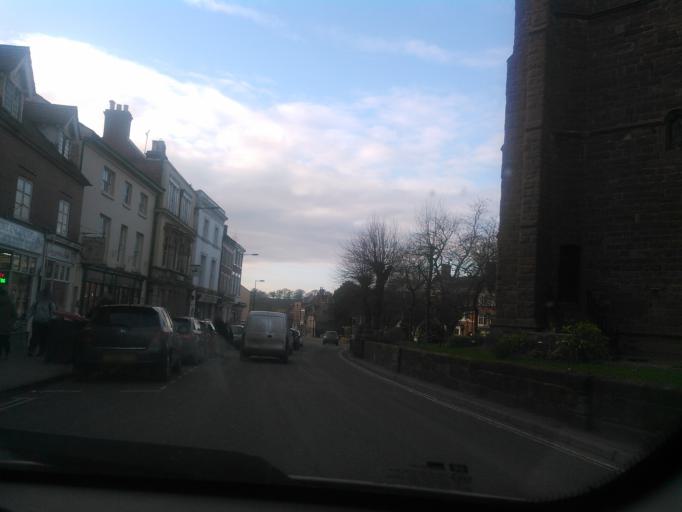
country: GB
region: England
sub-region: Telford and Wrekin
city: Newport
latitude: 52.7695
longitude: -2.3795
